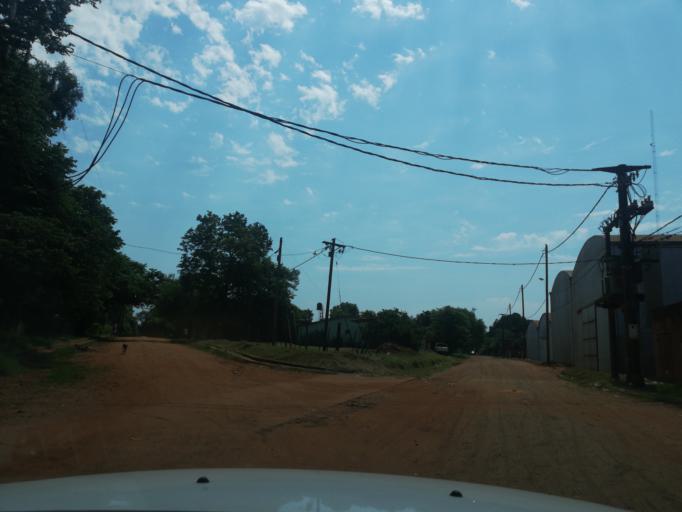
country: AR
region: Misiones
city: Garupa
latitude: -27.4401
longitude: -55.8866
